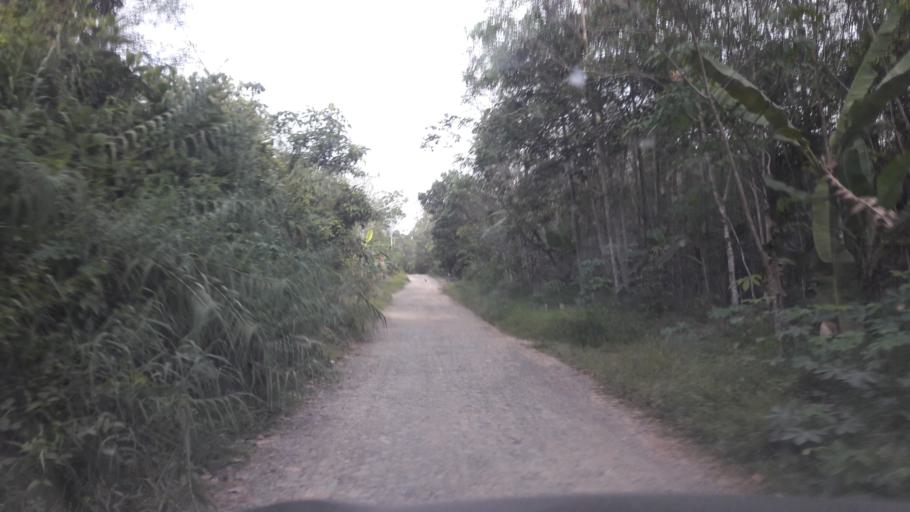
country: ID
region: South Sumatra
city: Gunungmenang
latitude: -3.2465
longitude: 104.0100
